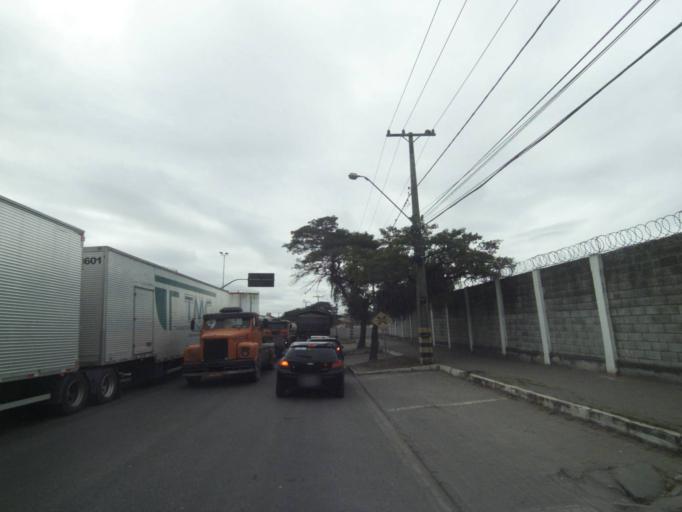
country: BR
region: Parana
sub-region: Paranagua
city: Paranagua
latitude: -25.5143
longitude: -48.5270
